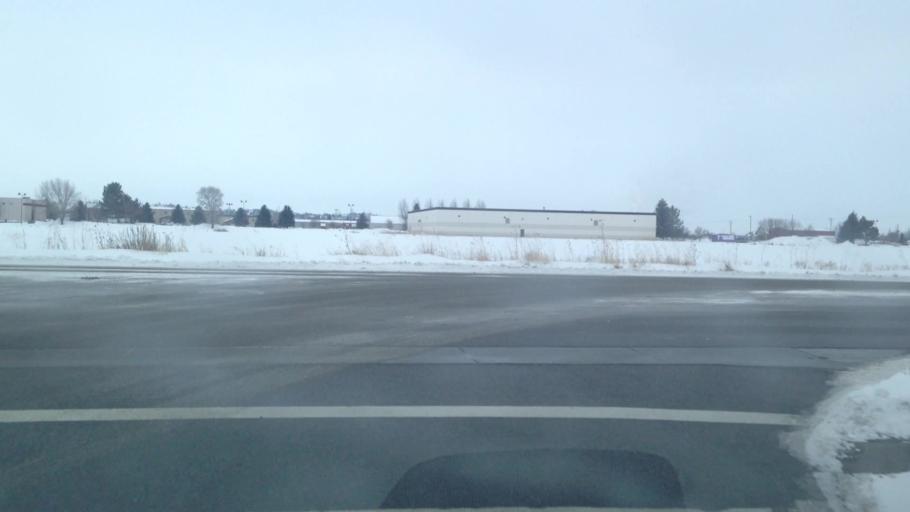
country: US
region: Idaho
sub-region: Madison County
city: Sugar City
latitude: 43.8551
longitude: -111.7747
